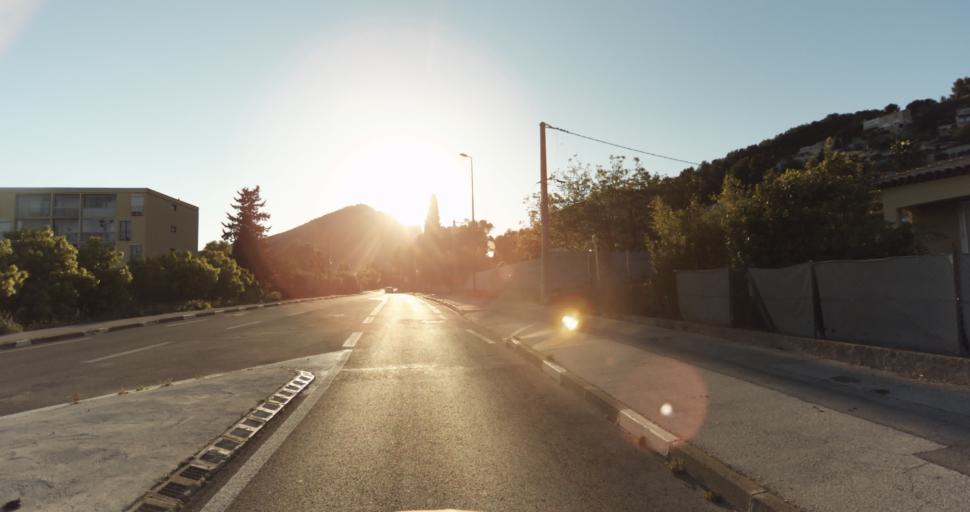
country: FR
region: Provence-Alpes-Cote d'Azur
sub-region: Departement du Var
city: La Valette-du-Var
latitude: 43.1427
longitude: 5.9945
